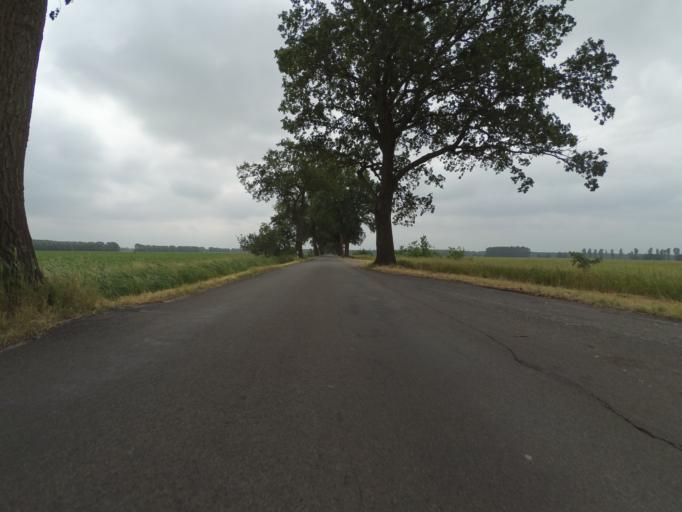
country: DE
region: Mecklenburg-Vorpommern
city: Neustadt-Glewe
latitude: 53.4244
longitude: 11.5542
